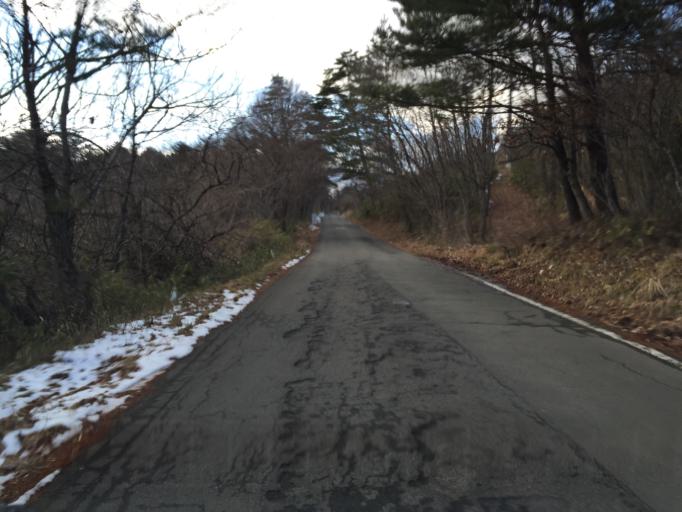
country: JP
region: Fukushima
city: Nihommatsu
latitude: 37.6758
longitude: 140.3667
